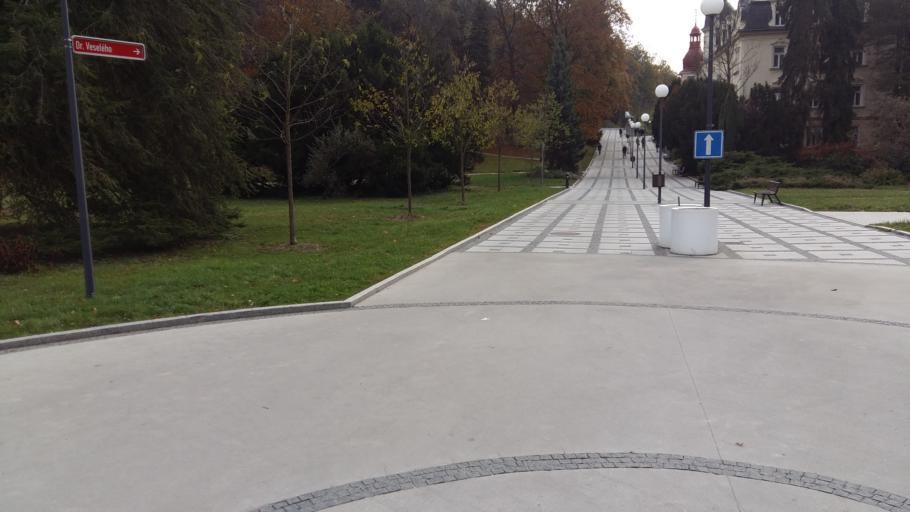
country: CZ
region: Zlin
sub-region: Okres Zlin
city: Luhacovice
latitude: 49.1049
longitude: 17.7595
